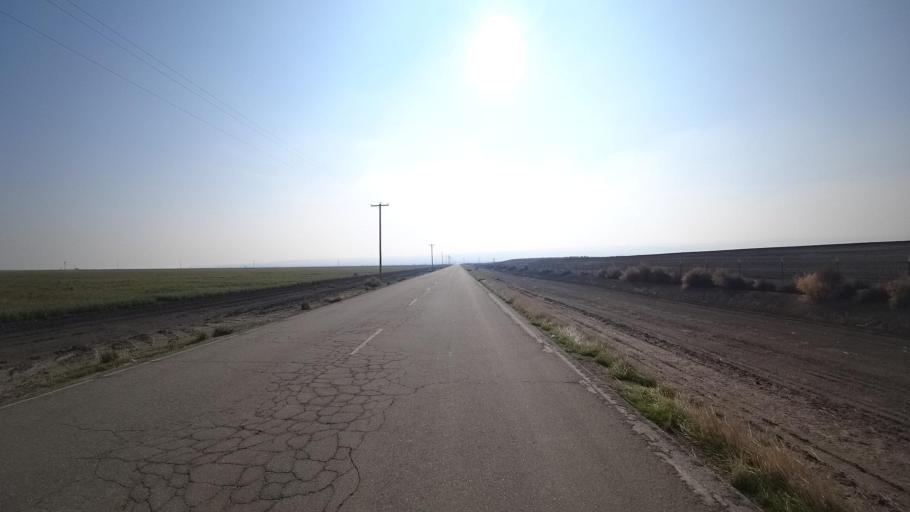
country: US
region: California
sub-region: Kern County
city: Buttonwillow
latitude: 35.3301
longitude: -119.3768
